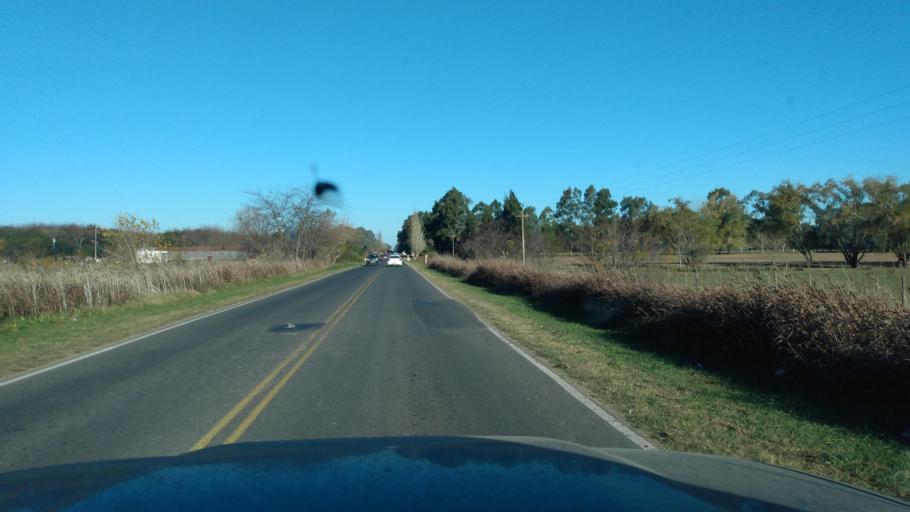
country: AR
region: Buenos Aires
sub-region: Partido de Lujan
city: Lujan
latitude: -34.5256
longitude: -59.1718
